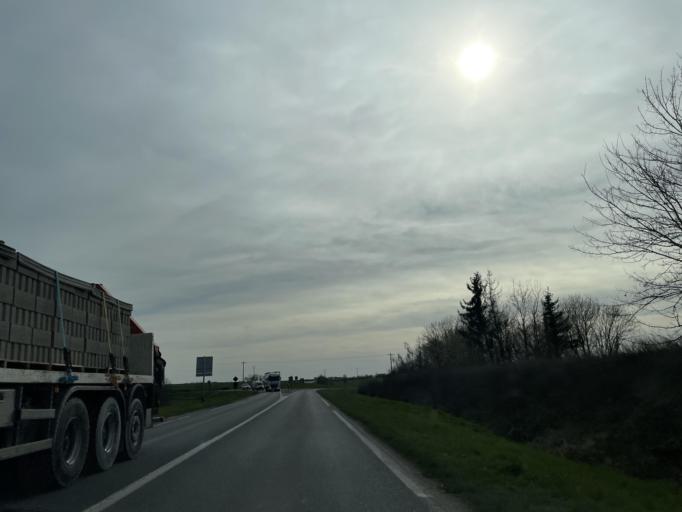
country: FR
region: Ile-de-France
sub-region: Departement de Seine-et-Marne
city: Jouy-le-Chatel
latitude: 48.6698
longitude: 3.1297
